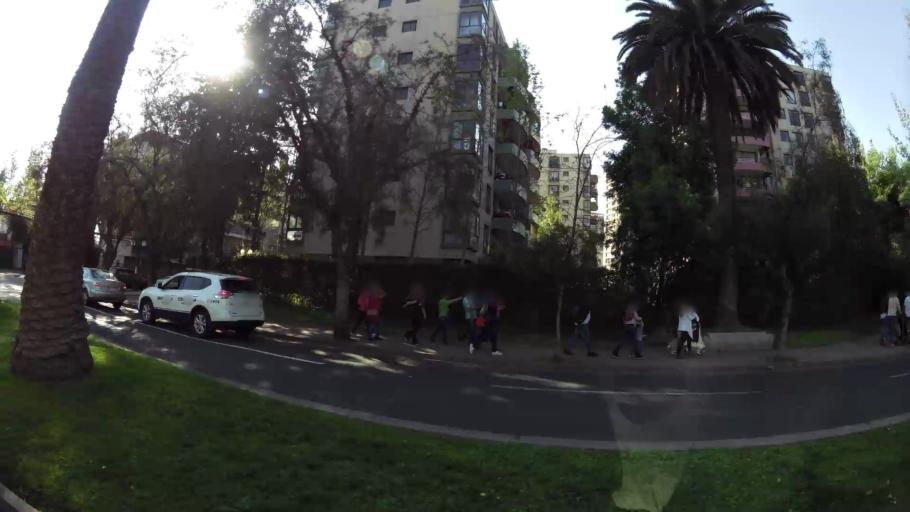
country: CL
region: Santiago Metropolitan
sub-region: Provincia de Santiago
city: Villa Presidente Frei, Nunoa, Santiago, Chile
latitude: -33.4421
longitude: -70.6125
